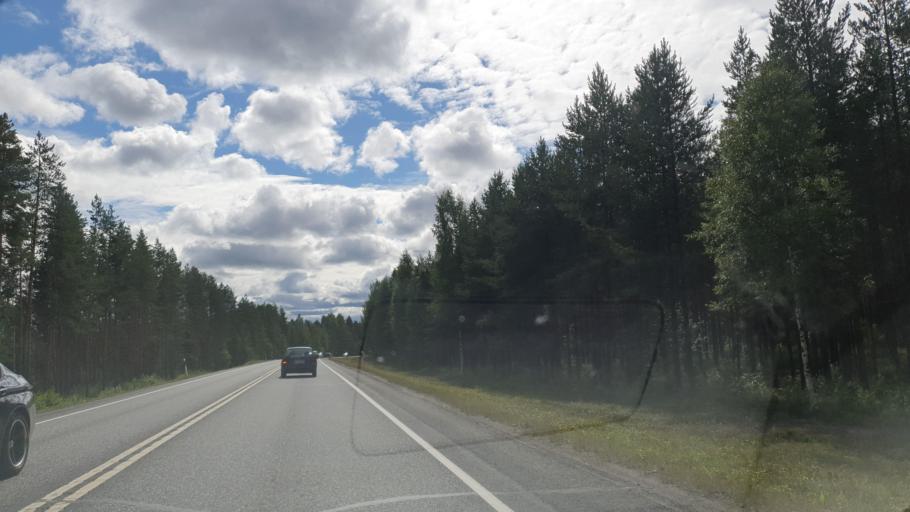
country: FI
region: Kainuu
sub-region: Kajaani
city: Kajaani
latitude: 64.1403
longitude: 27.4968
